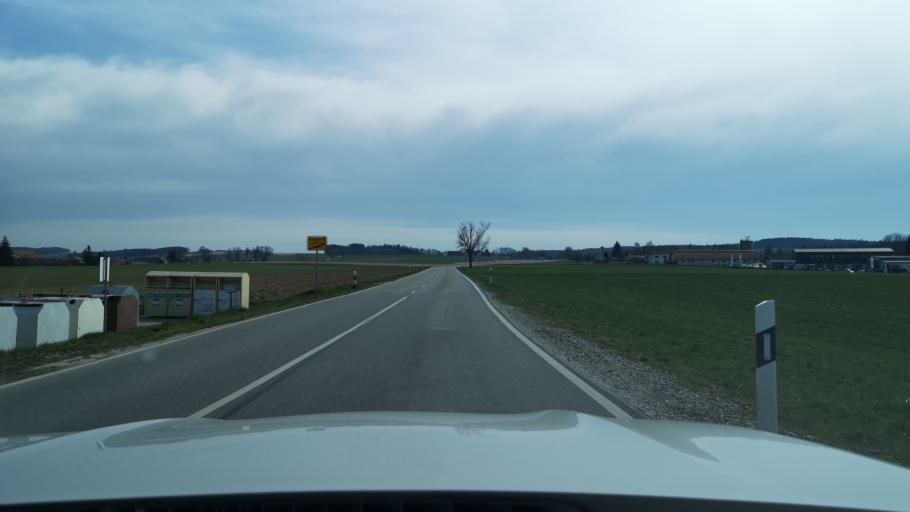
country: DE
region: Bavaria
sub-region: Upper Bavaria
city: Isen
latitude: 48.2044
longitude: 12.0529
